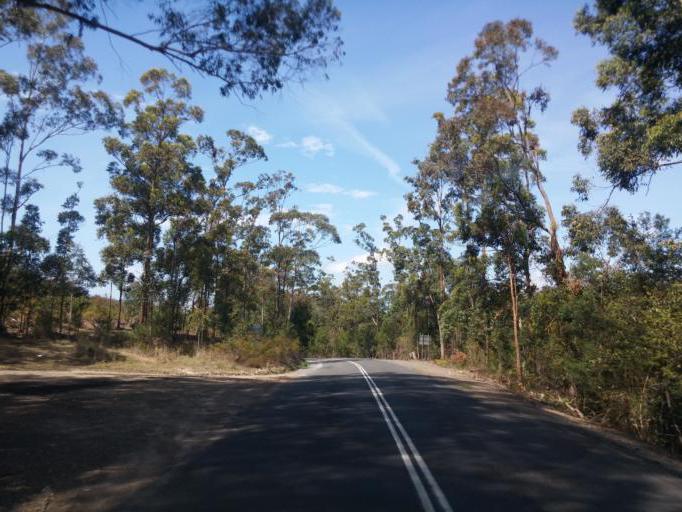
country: AU
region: New South Wales
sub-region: Great Lakes
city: Bulahdelah
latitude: -32.3904
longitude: 152.2505
